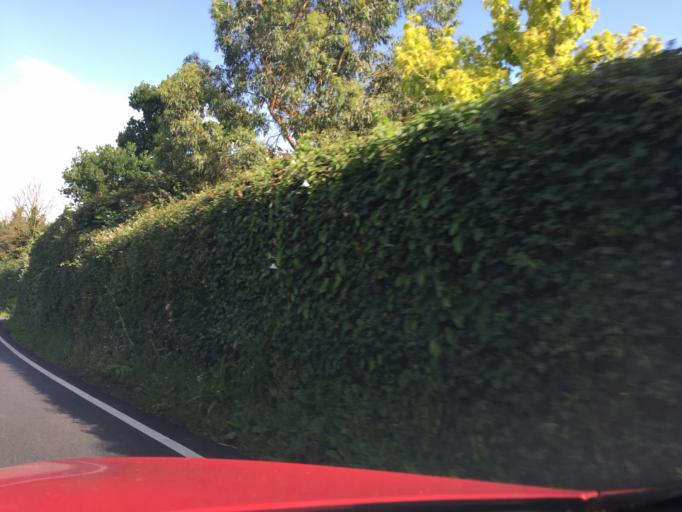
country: GB
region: England
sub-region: Gloucestershire
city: Stonehouse
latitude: 51.8063
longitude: -2.2943
